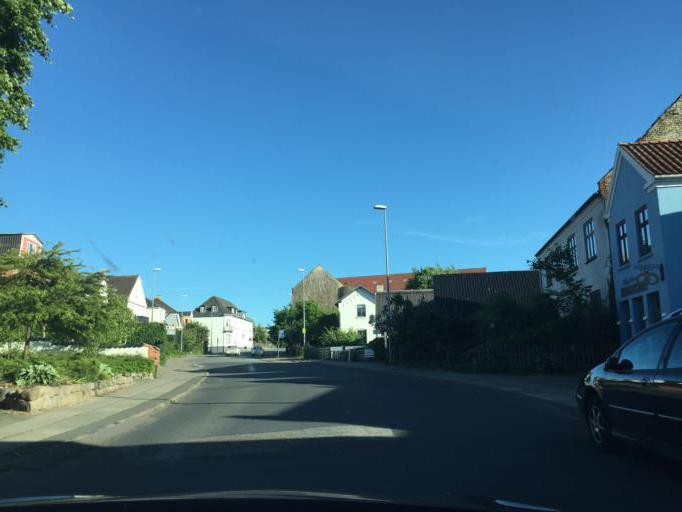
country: DK
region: Zealand
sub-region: Slagelse Kommune
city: Slagelse
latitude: 55.4095
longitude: 11.3519
